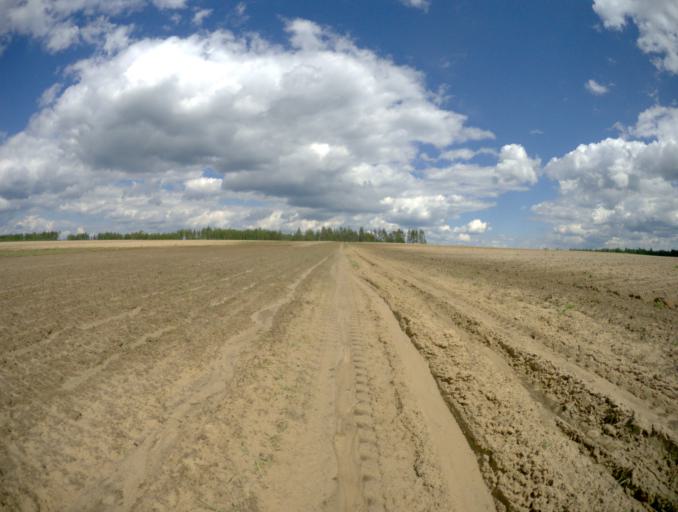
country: RU
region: Vladimir
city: Velikodvorskiy
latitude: 55.2727
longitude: 40.8391
